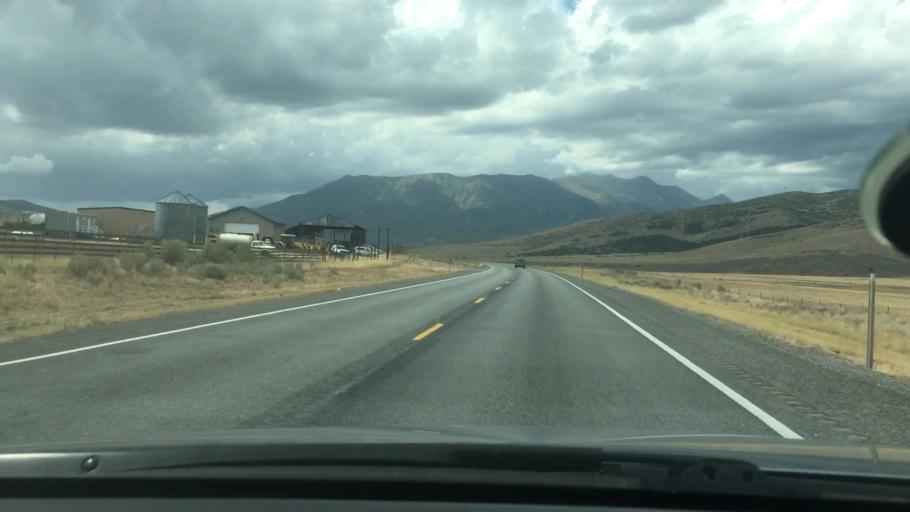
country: US
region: Utah
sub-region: Sanpete County
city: Fountain Green
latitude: 39.6748
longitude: -111.6663
